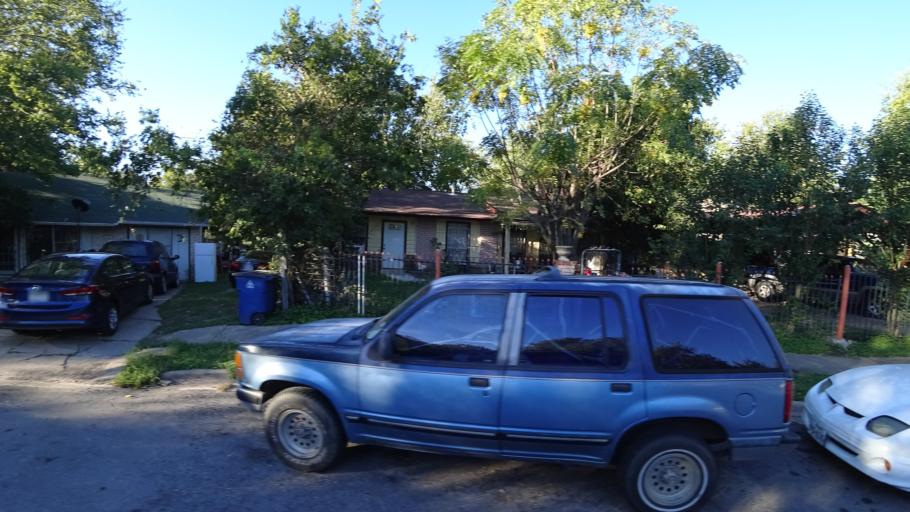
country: US
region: Texas
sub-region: Travis County
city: Hornsby Bend
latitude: 30.3053
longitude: -97.6436
